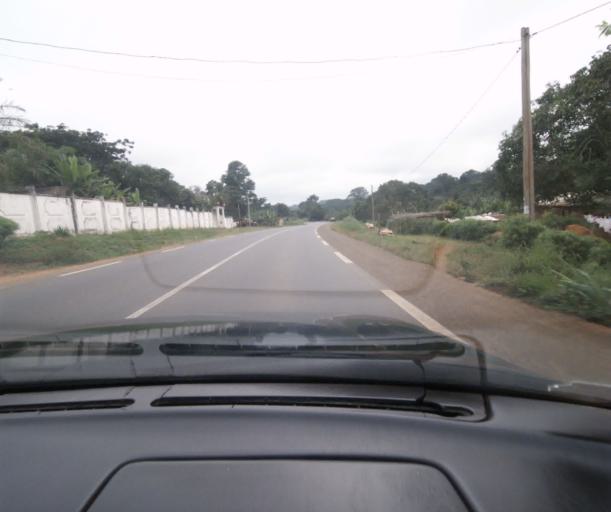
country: CM
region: Centre
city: Obala
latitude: 4.2010
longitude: 11.4501
